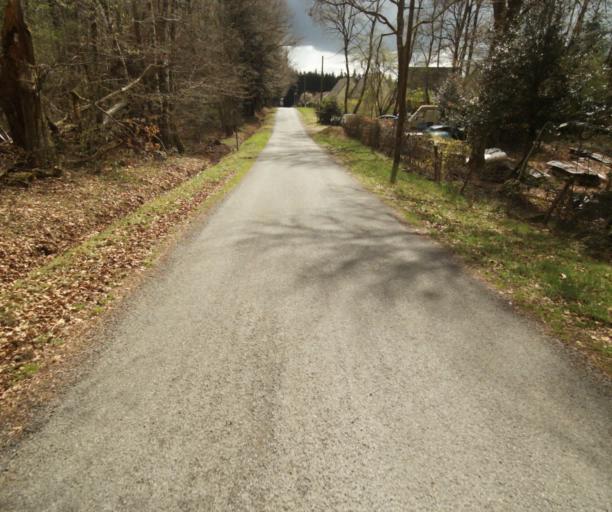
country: FR
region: Limousin
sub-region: Departement de la Correze
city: Correze
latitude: 45.2734
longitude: 1.9804
